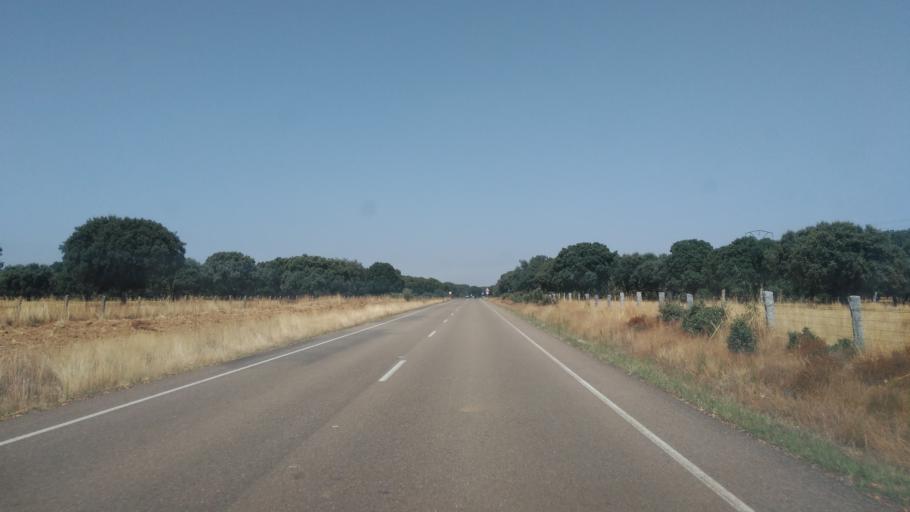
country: ES
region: Castille and Leon
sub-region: Provincia de Salamanca
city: Abusejo
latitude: 40.6803
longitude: -6.1288
